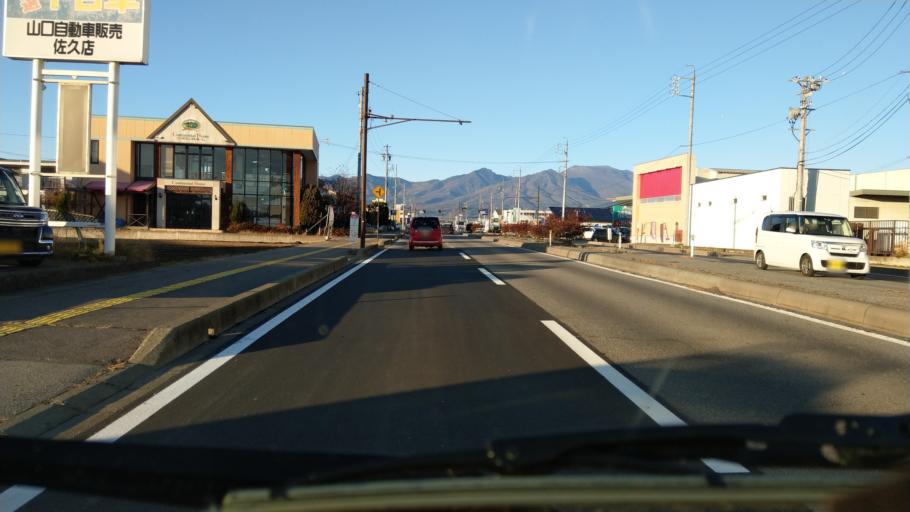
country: JP
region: Nagano
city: Saku
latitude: 36.2501
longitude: 138.4676
